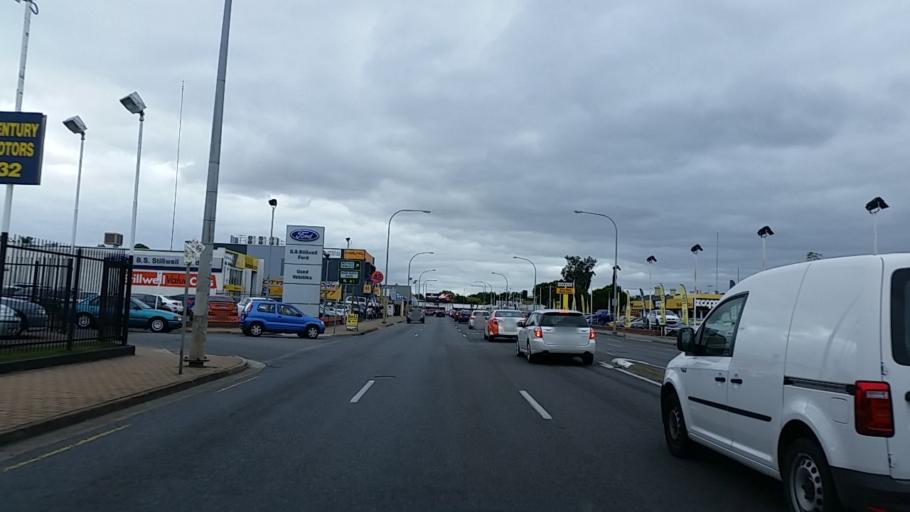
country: AU
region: South Australia
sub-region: Adelaide
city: North Adelaide
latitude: -34.8956
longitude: 138.6008
